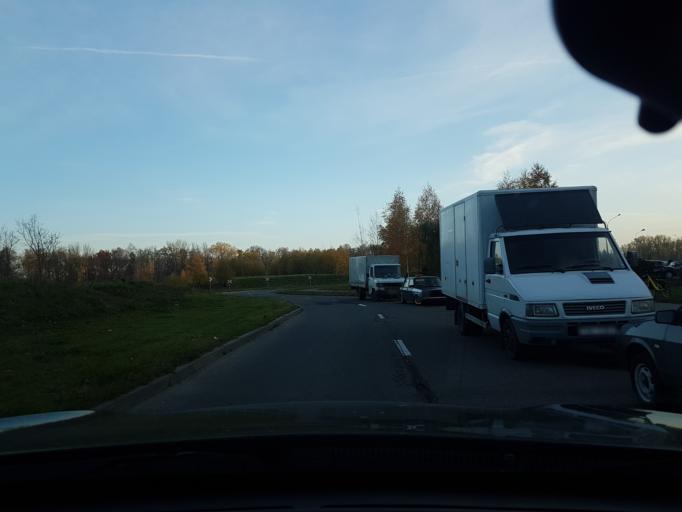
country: BY
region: Minsk
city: Yubilyeyny
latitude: 53.8493
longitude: 27.4902
